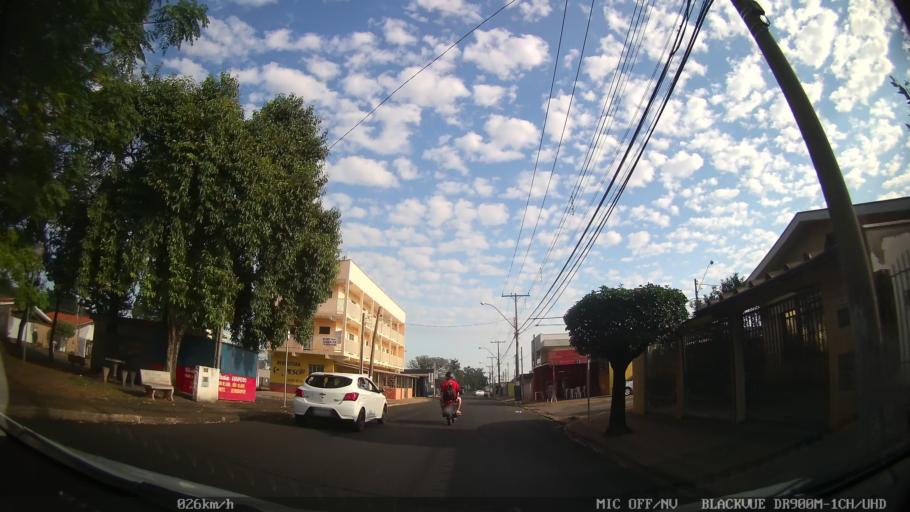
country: BR
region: Sao Paulo
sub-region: Americana
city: Americana
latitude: -22.7385
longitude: -47.3555
